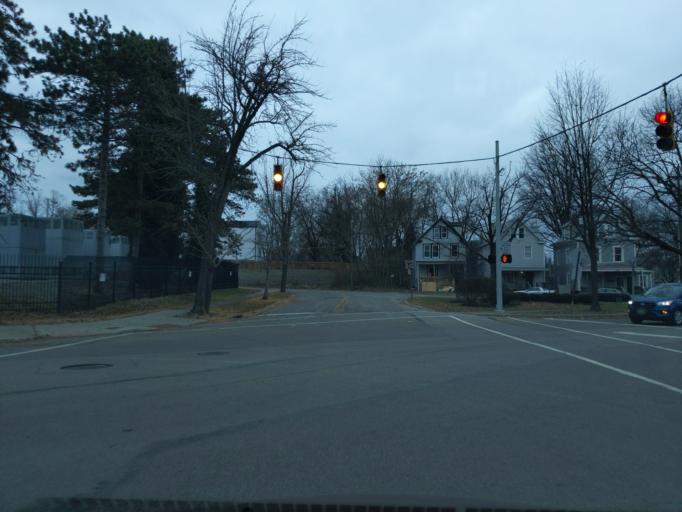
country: US
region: Kentucky
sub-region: Campbell County
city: Dayton
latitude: 39.1291
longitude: -84.4827
